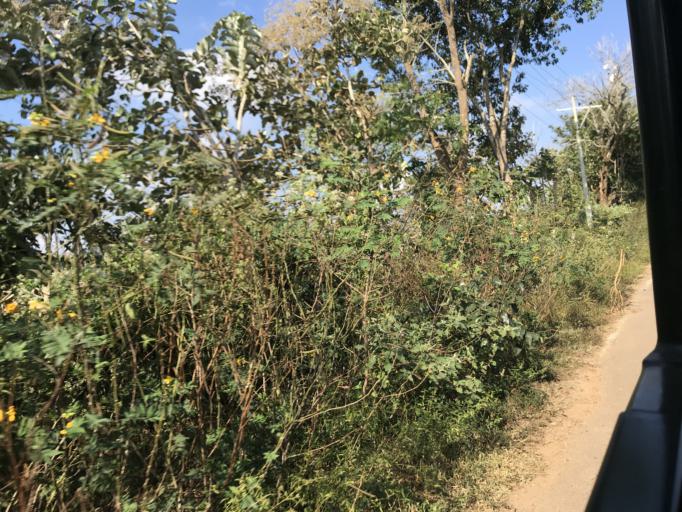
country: IN
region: Karnataka
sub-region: Mysore
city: Sargur
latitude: 11.9432
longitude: 76.2677
